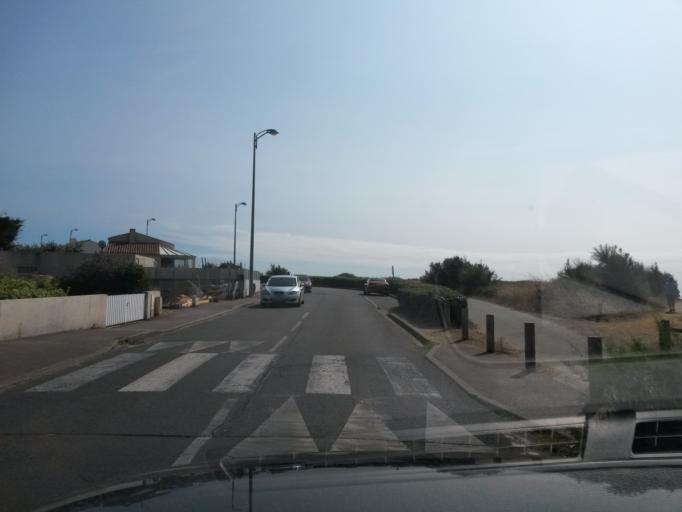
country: FR
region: Pays de la Loire
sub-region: Departement de la Vendee
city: Bretignolles-sur-Mer
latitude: 46.6210
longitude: -1.8722
